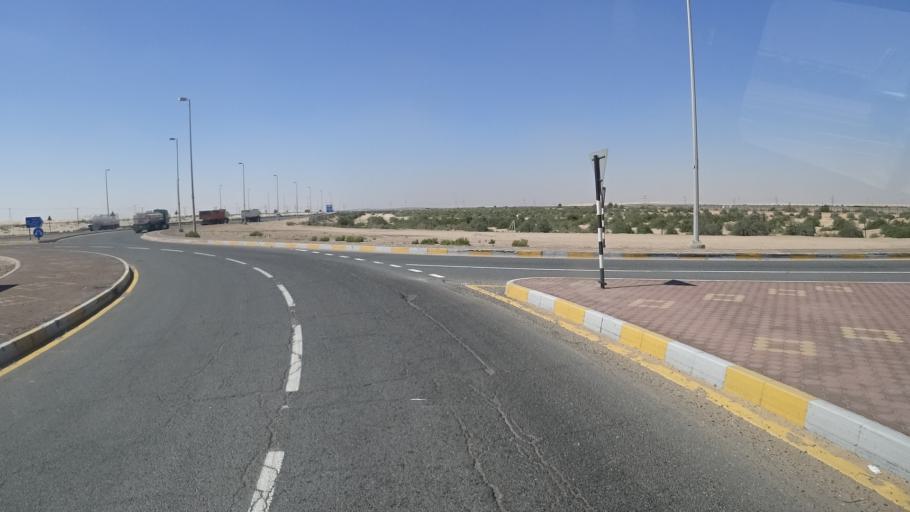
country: AE
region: Abu Dhabi
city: Abu Dhabi
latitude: 24.2099
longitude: 54.8214
